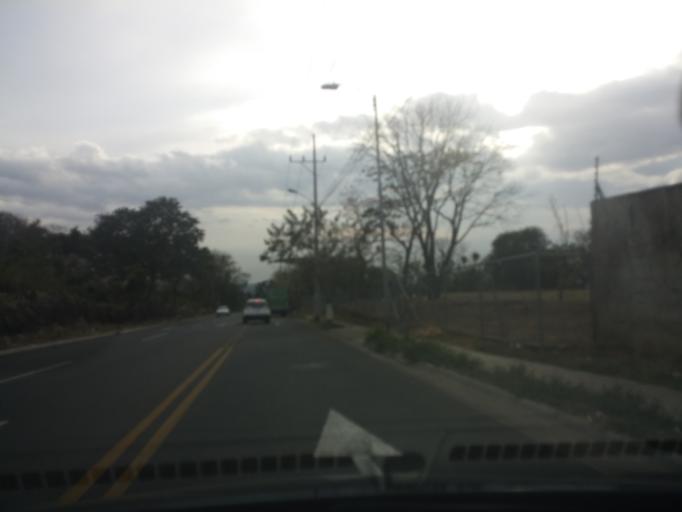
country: CR
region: Heredia
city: San Francisco
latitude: 9.9896
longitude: -84.1427
